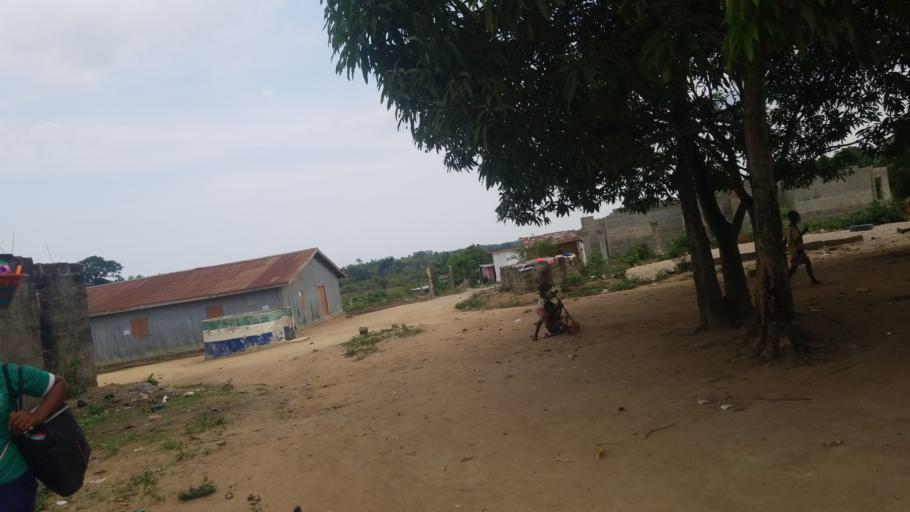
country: SL
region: Western Area
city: Waterloo
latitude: 8.3153
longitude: -13.0434
